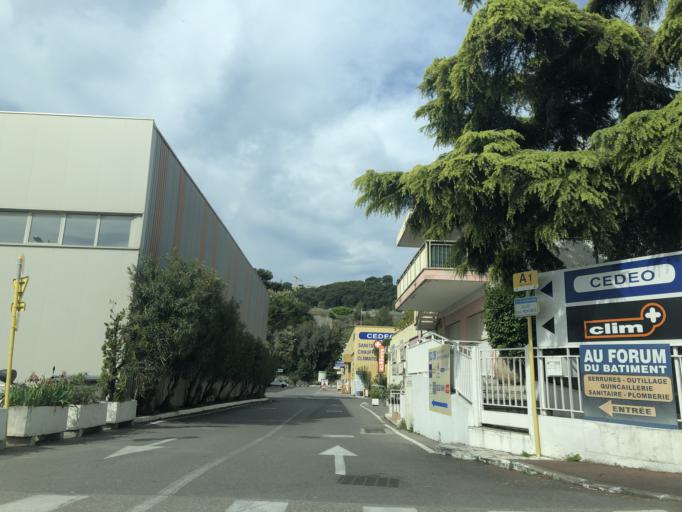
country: FR
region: Provence-Alpes-Cote d'Azur
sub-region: Departement des Alpes-Maritimes
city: Saint-Laurent-du-Var
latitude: 43.6840
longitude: 7.1883
